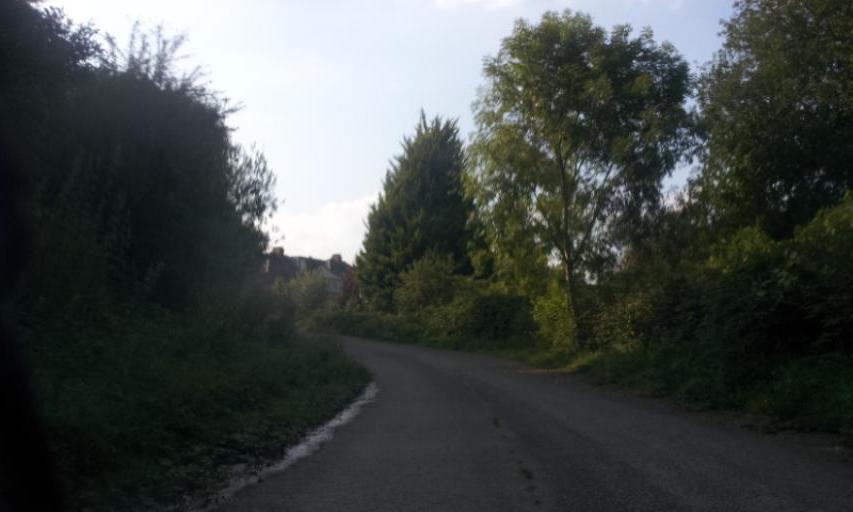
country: GB
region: England
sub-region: Kent
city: Boxley
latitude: 51.3008
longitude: 0.5159
